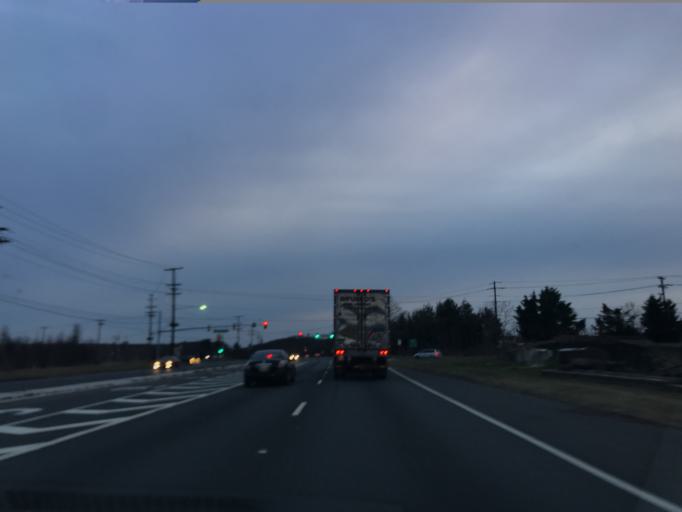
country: US
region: New Jersey
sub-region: Middlesex County
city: Dayton
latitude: 40.4026
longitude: -74.5085
